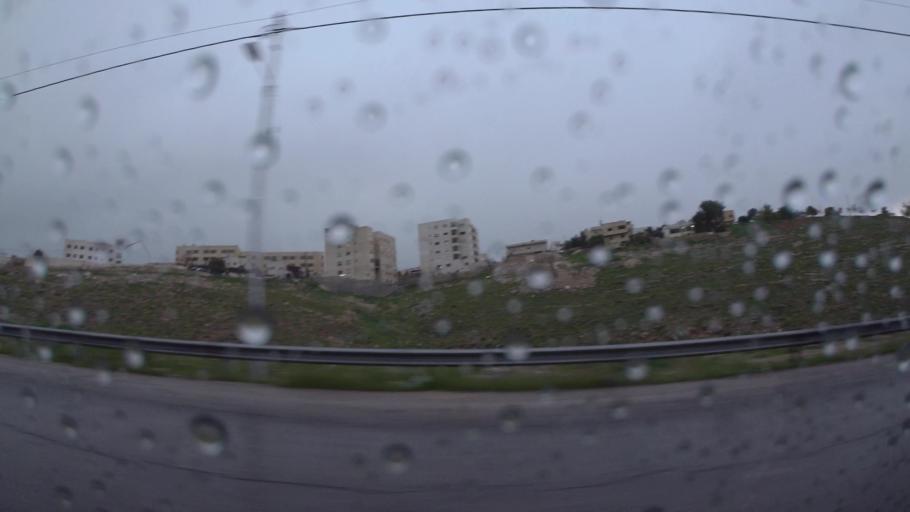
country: JO
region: Amman
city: Amman
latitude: 31.9974
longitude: 35.9694
